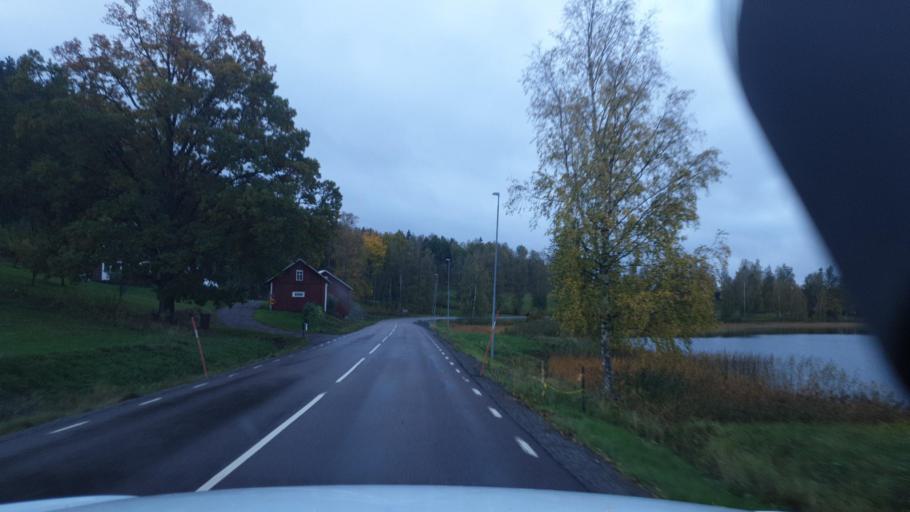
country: SE
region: Vaermland
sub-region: Arvika Kommun
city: Arvika
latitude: 59.7841
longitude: 12.6205
